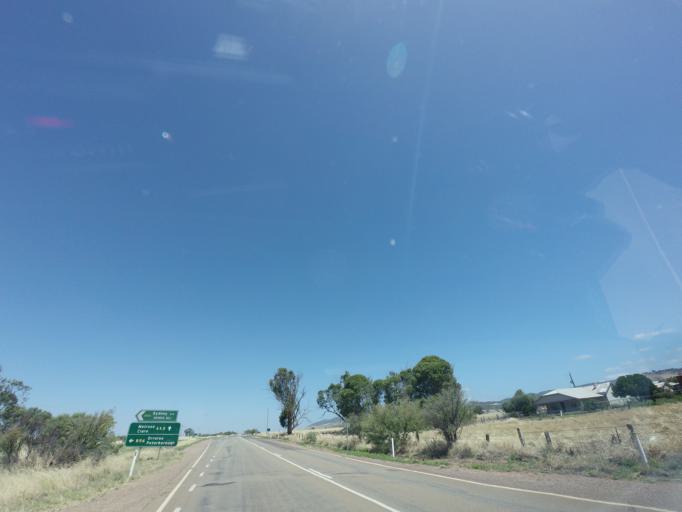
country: AU
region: South Australia
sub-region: Flinders Ranges
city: Quorn
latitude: -32.6647
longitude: 138.1104
